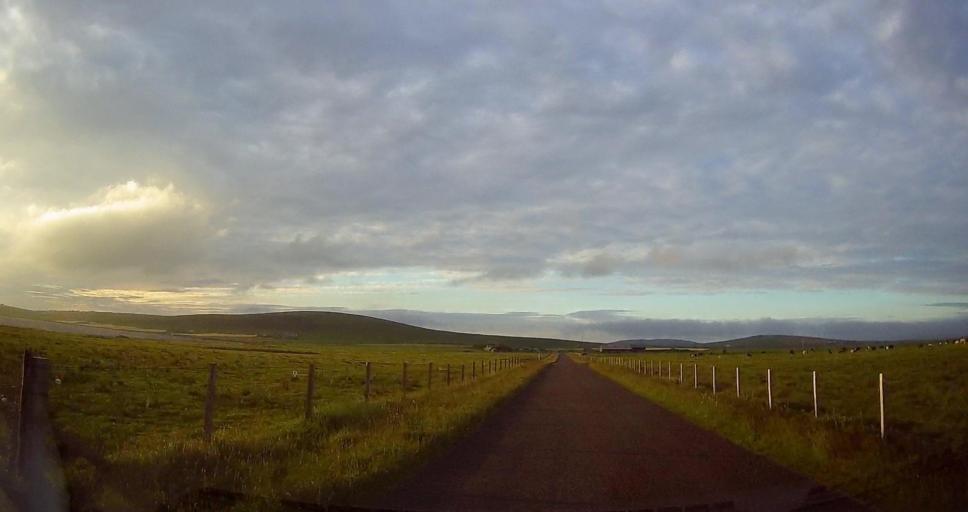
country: GB
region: Scotland
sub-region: Orkney Islands
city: Stromness
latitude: 59.1043
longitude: -3.2571
